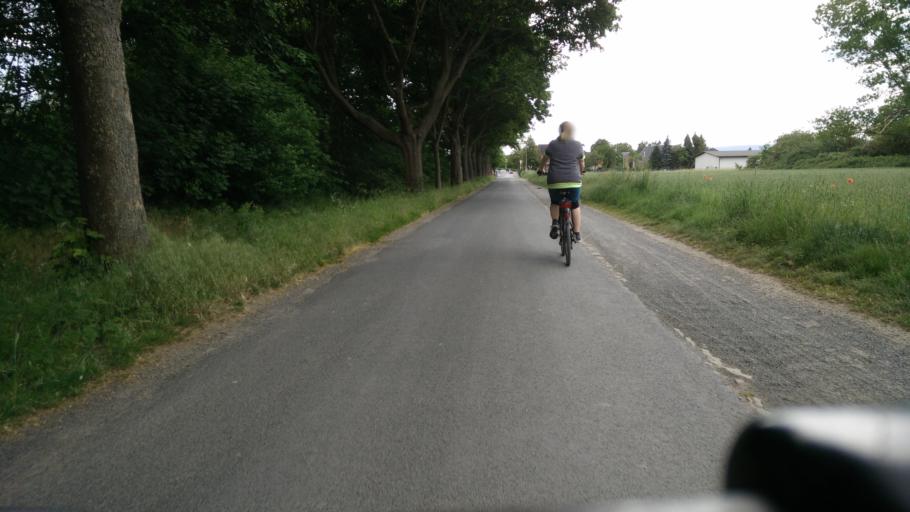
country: DE
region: Lower Saxony
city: Wunstorf
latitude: 52.4317
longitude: 9.4132
